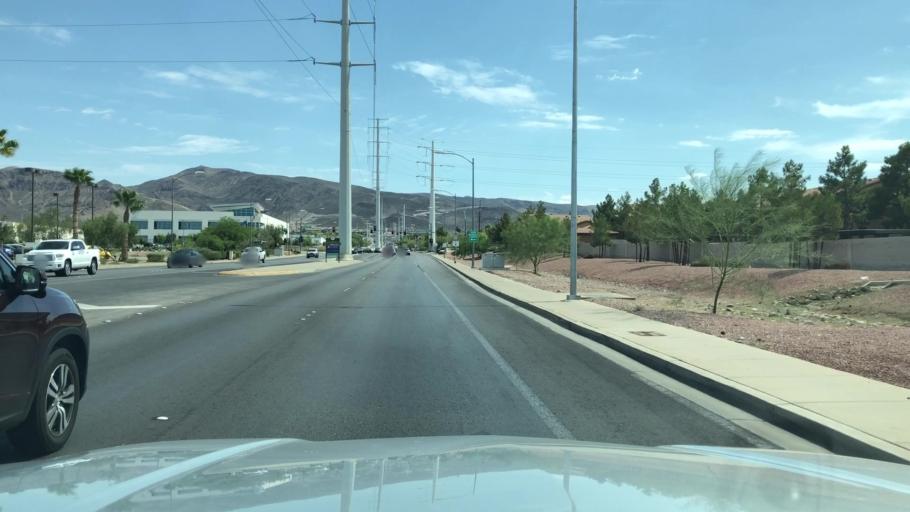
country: US
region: Nevada
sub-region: Clark County
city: Henderson
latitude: 36.0441
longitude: -115.0294
